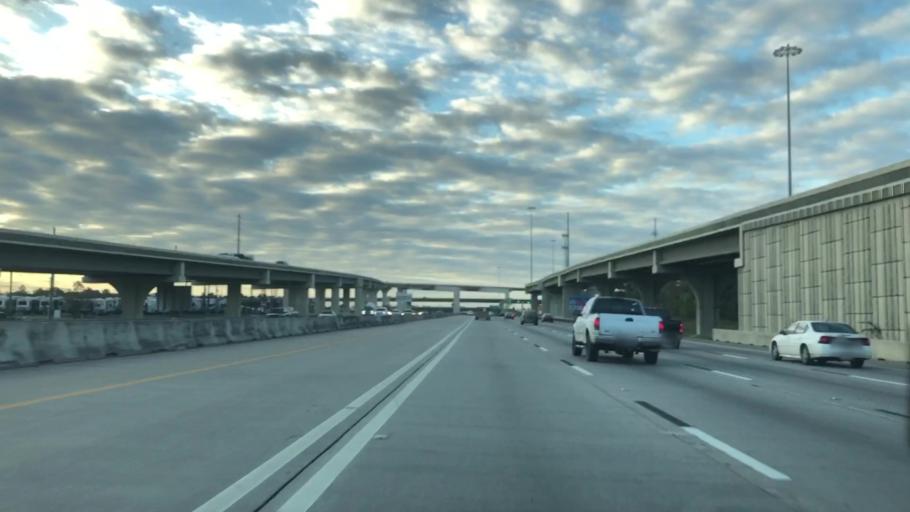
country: US
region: Texas
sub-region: Harris County
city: Spring
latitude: 30.0987
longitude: -95.4356
